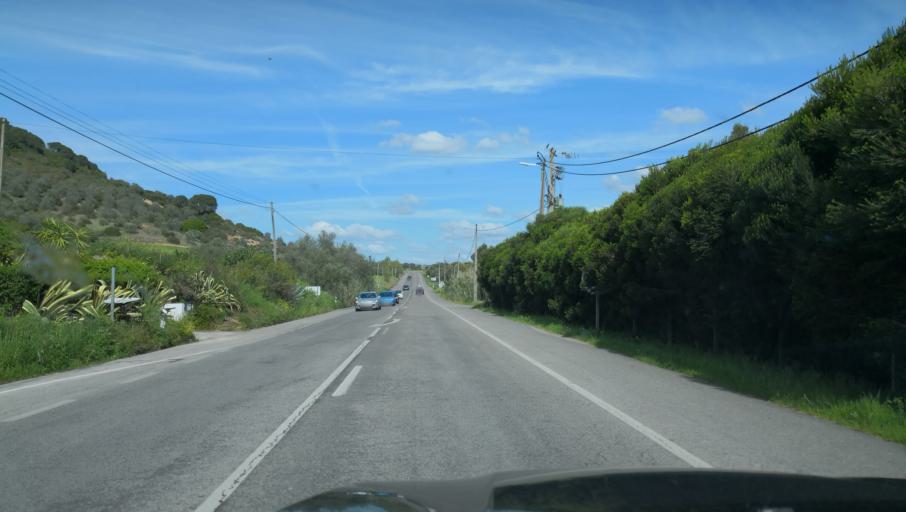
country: PT
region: Setubal
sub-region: Palmela
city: Quinta do Anjo
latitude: 38.5227
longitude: -8.9583
